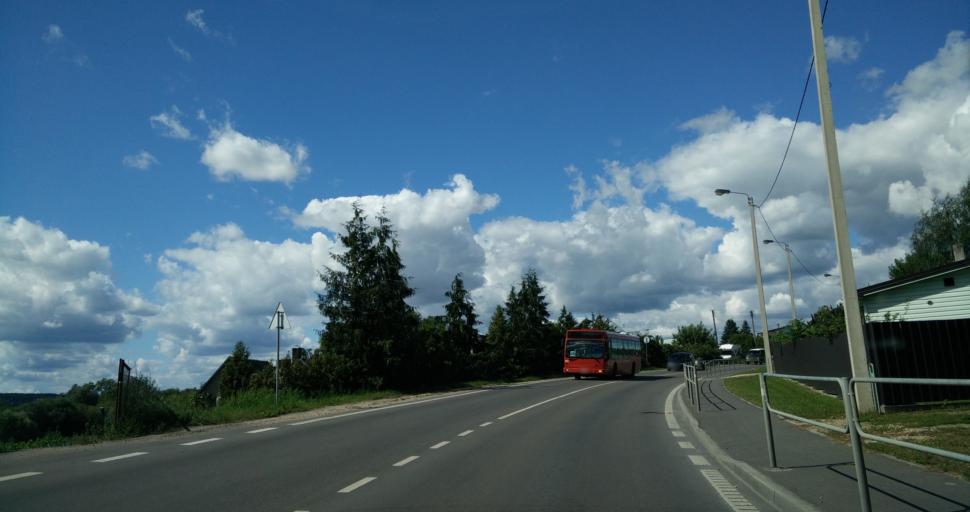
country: LT
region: Kauno apskritis
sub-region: Kauno rajonas
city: Akademija (Kaunas)
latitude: 54.9230
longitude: 23.7944
